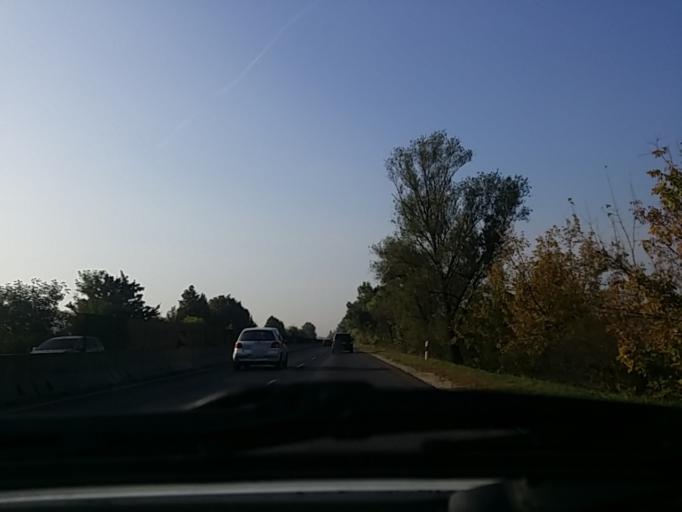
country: HU
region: Pest
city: Budakalasz
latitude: 47.6309
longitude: 19.0700
